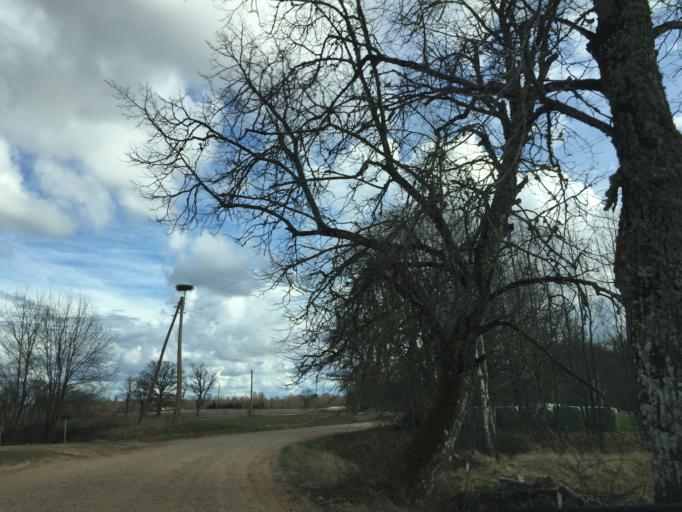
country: LV
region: Limbazu Rajons
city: Limbazi
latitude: 57.6123
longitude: 24.7421
